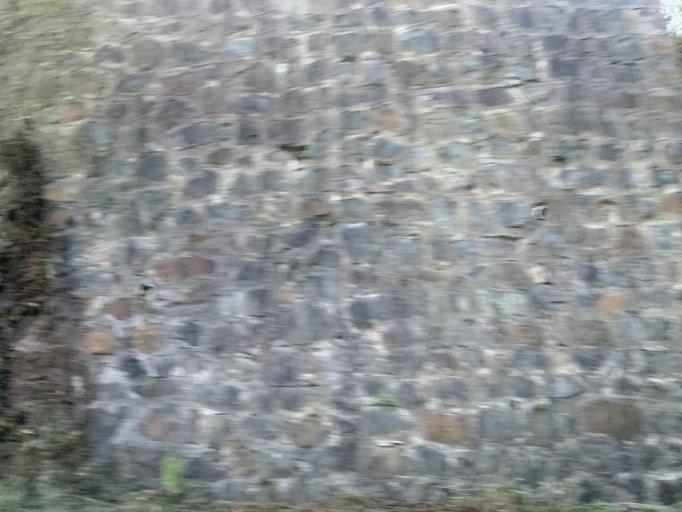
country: TR
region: Trabzon
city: Dernekpazari
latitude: 40.8651
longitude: 40.2787
